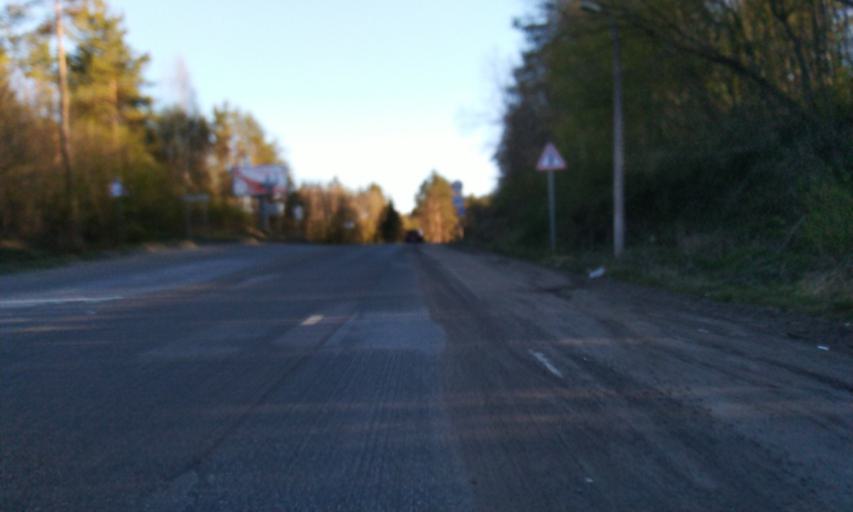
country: RU
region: Leningrad
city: Toksovo
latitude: 60.1350
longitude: 30.5275
